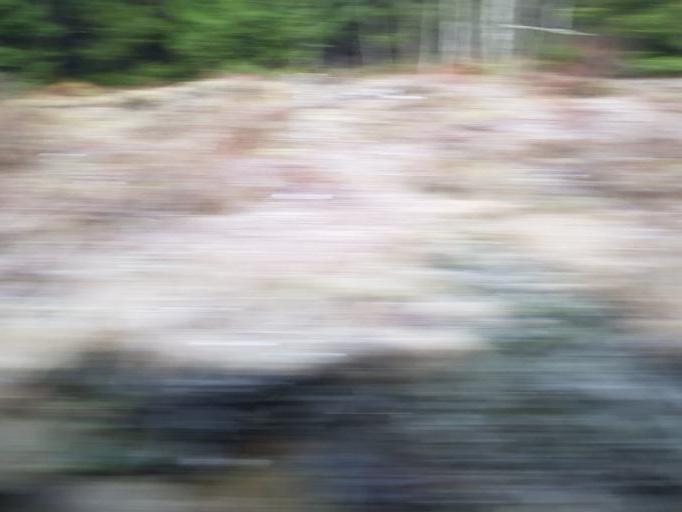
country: NO
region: Sor-Trondelag
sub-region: Midtre Gauldal
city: Storen
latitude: 62.9925
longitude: 10.2461
